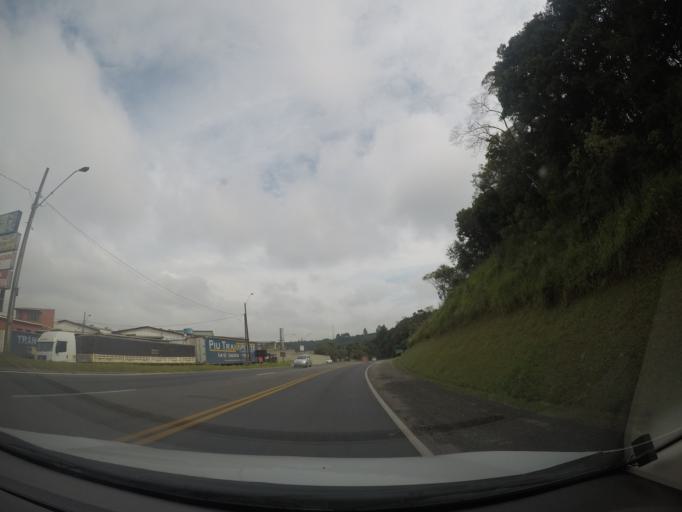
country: BR
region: Parana
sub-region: Colombo
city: Colombo
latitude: -25.3428
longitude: -49.2218
